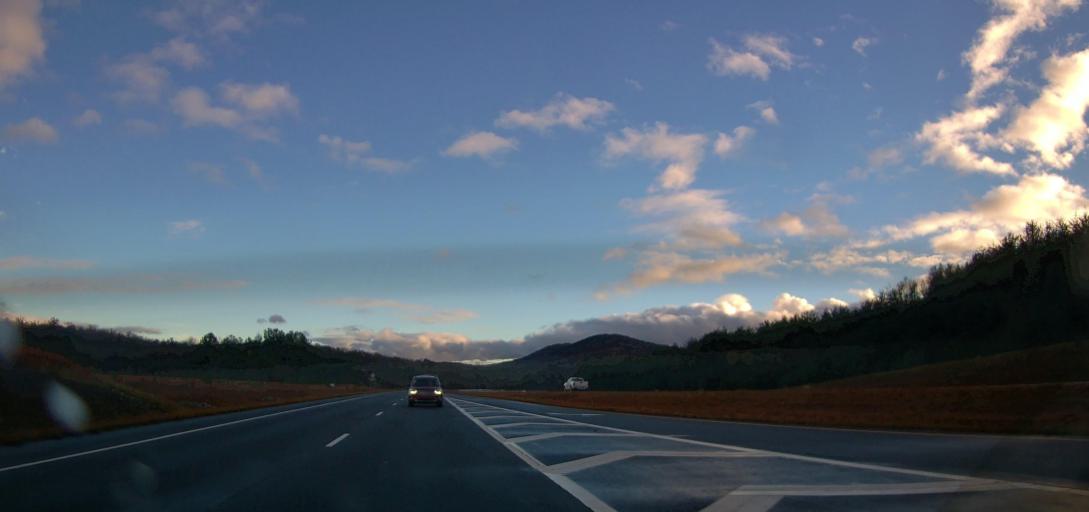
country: US
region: Georgia
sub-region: White County
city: Cleveland
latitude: 34.6037
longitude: -83.7821
